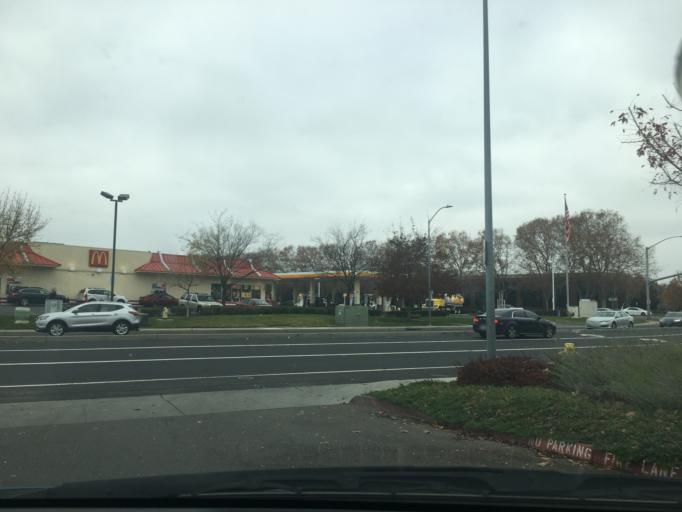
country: US
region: California
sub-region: Yolo County
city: West Sacramento
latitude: 38.5908
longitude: -121.5487
